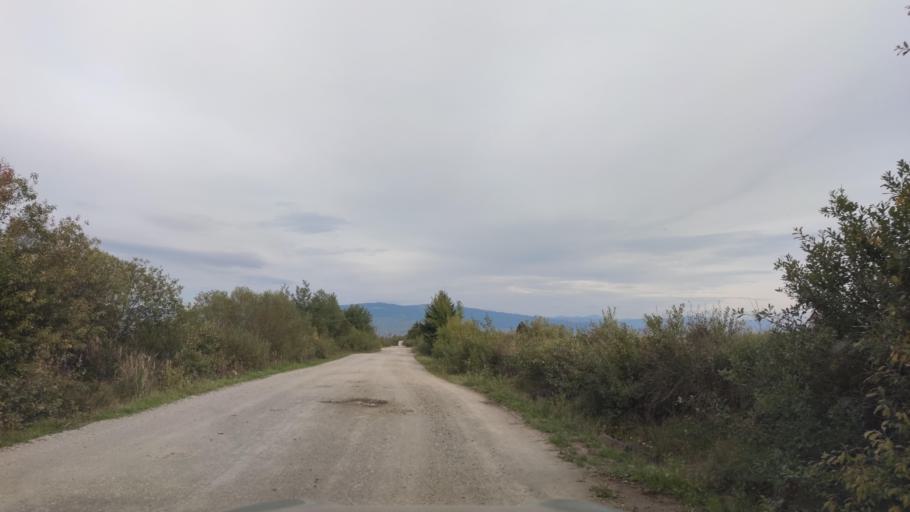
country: RO
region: Harghita
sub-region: Comuna Remetea
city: Remetea
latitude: 46.8119
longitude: 25.3768
